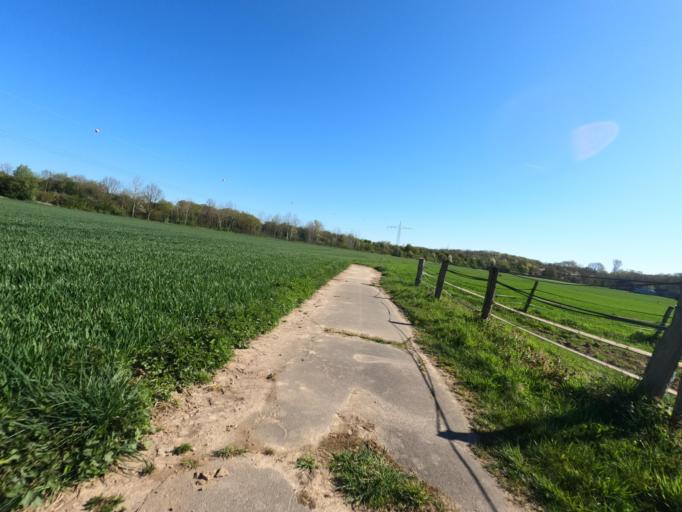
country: DE
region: North Rhine-Westphalia
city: Huckelhoven
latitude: 51.0679
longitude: 6.2180
